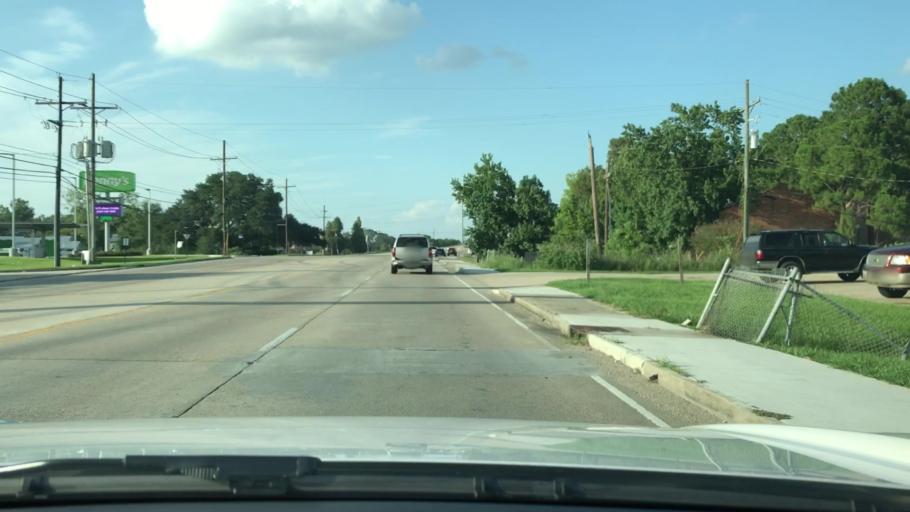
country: US
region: Louisiana
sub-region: East Baton Rouge Parish
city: Village Saint George
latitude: 30.3714
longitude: -91.0725
